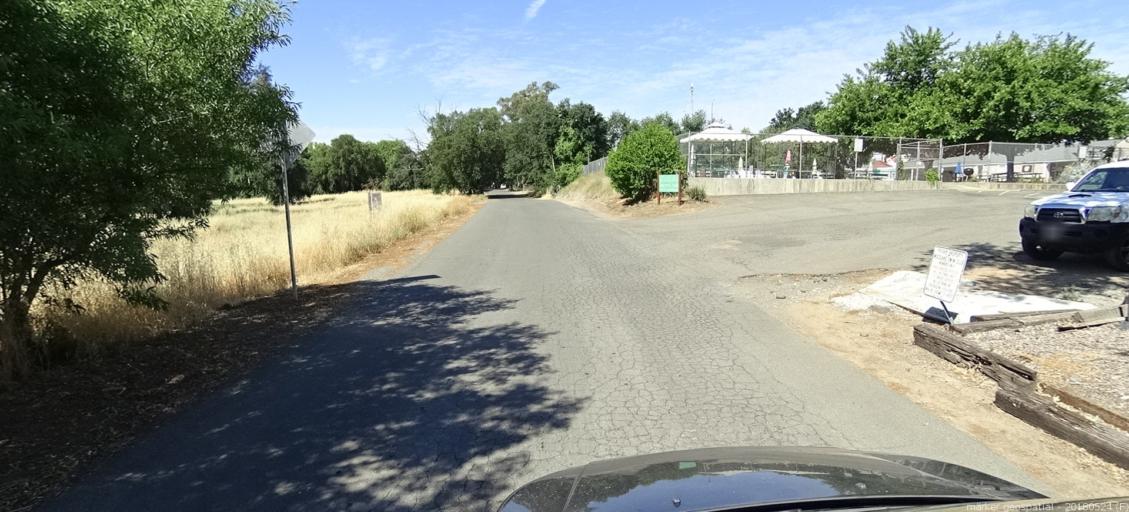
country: US
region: California
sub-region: Sacramento County
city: Sacramento
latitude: 38.6052
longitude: -121.4585
